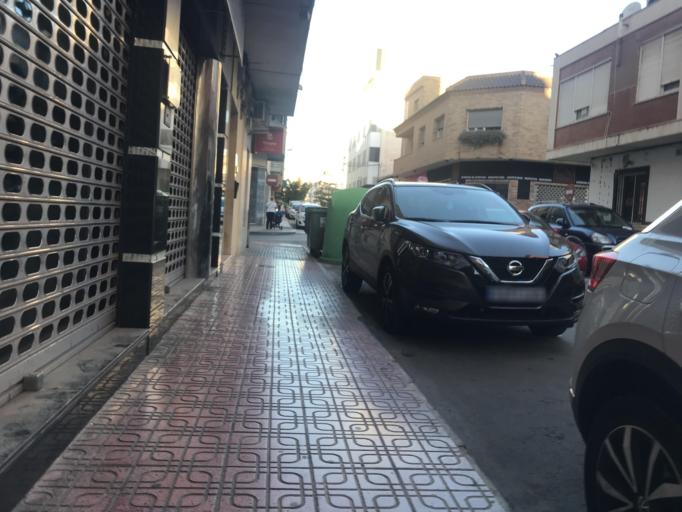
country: ES
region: Valencia
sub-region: Provincia de Alicante
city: Torrevieja
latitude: 37.9787
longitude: -0.6828
